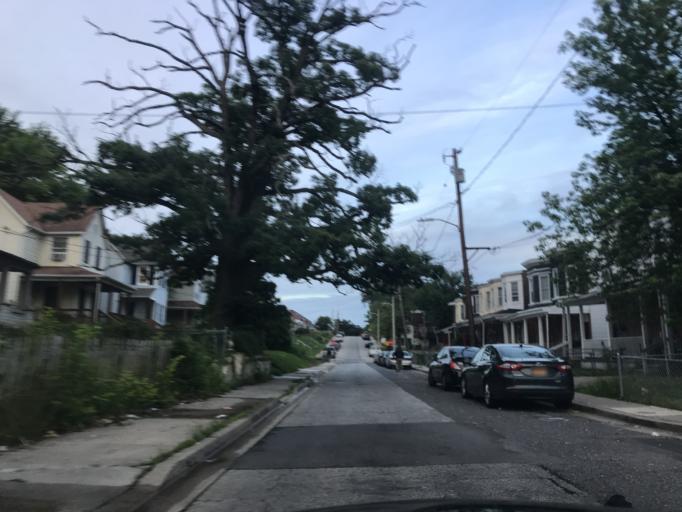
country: US
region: Maryland
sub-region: Baltimore County
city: Towson
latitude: 39.3535
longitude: -76.6067
